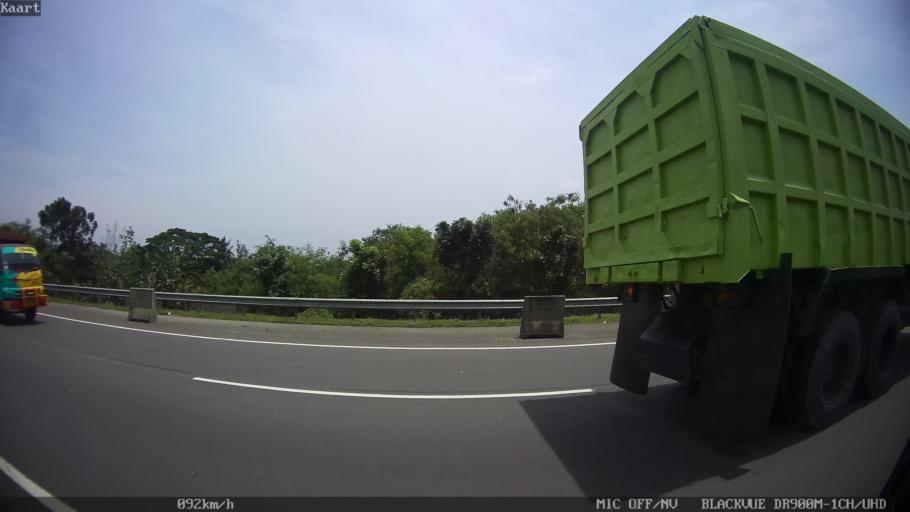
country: ID
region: West Java
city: Kresek
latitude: -6.1887
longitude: 106.4102
